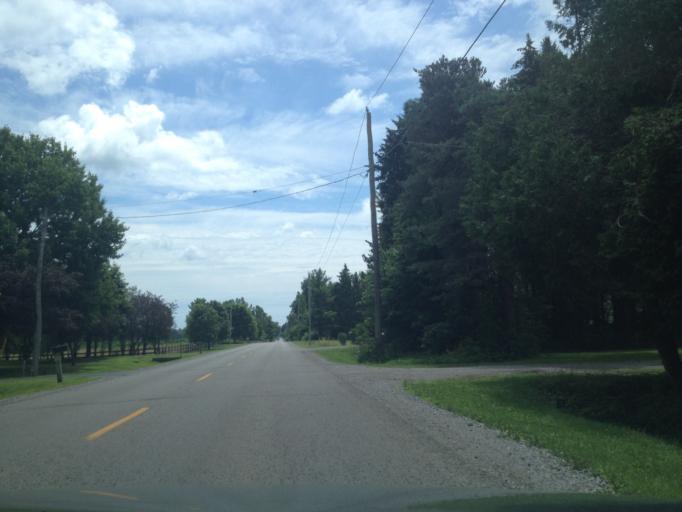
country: CA
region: Ontario
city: Norfolk County
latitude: 42.8037
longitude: -80.3154
